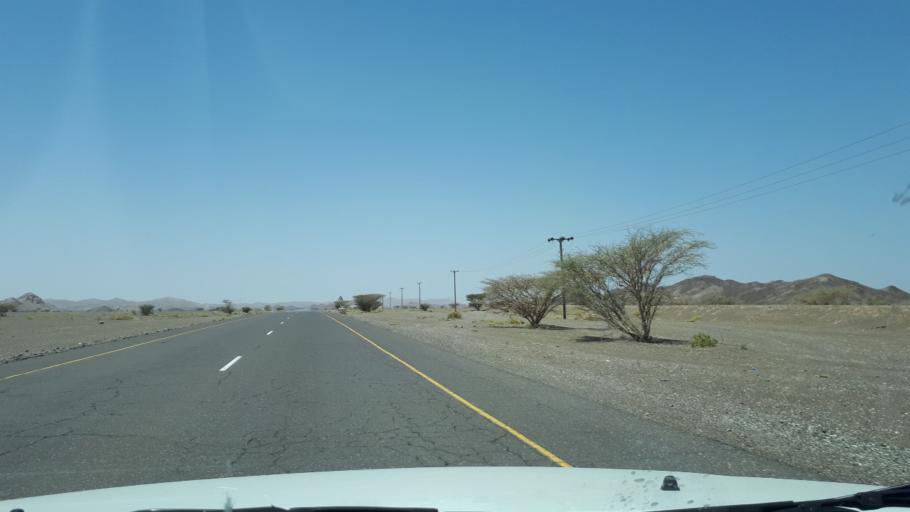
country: OM
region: Ash Sharqiyah
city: Ibra'
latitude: 22.6239
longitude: 58.4506
